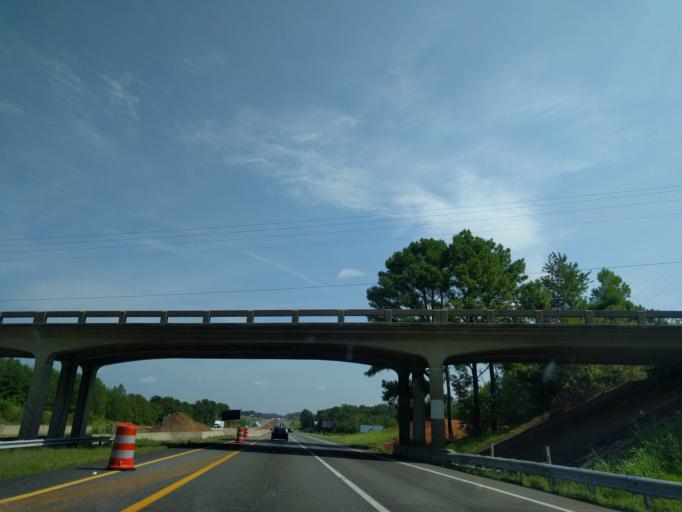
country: US
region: Tennessee
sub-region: Sumner County
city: Portland
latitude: 36.6195
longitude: -86.5772
